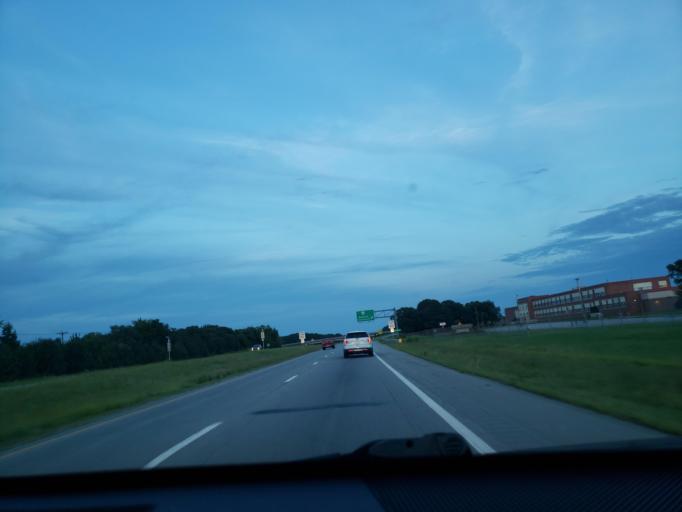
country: US
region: Virginia
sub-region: Southampton County
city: Courtland
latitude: 36.7019
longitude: -77.1058
